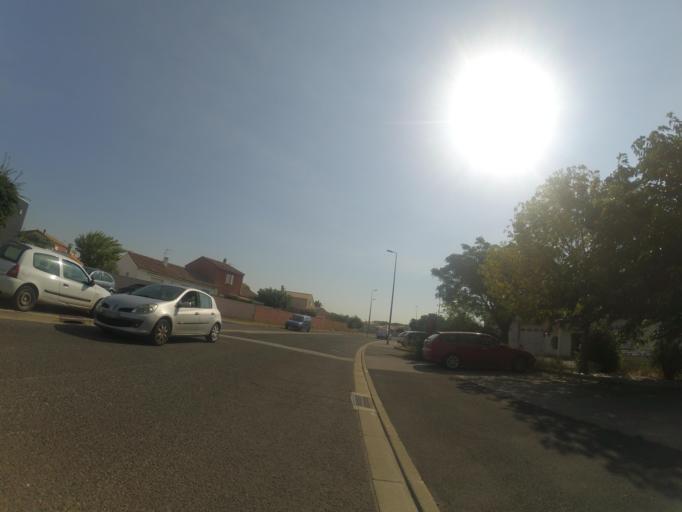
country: FR
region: Languedoc-Roussillon
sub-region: Departement des Pyrenees-Orientales
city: Toulouges
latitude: 42.6628
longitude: 2.8281
